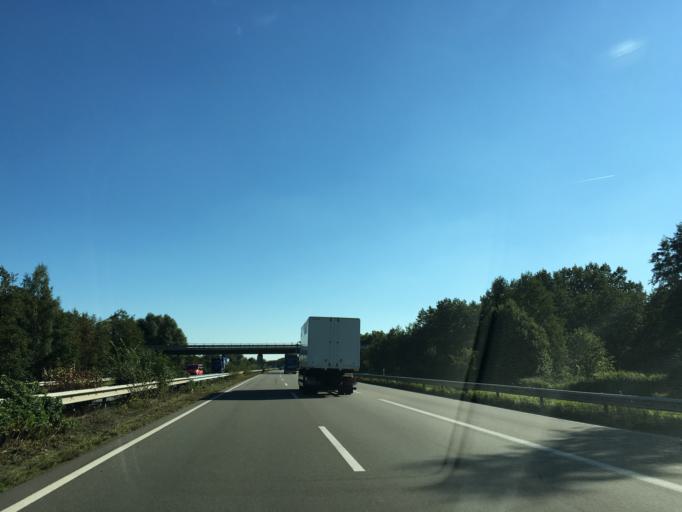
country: DE
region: Lower Saxony
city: Mechtersen
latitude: 53.3084
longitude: 10.3303
